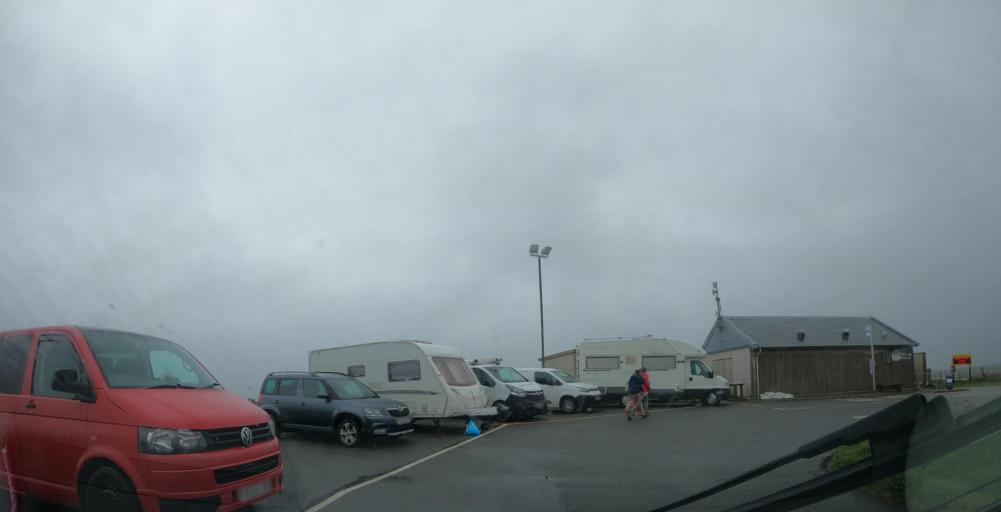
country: GB
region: Scotland
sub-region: Eilean Siar
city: Barra
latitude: 57.0086
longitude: -7.4047
